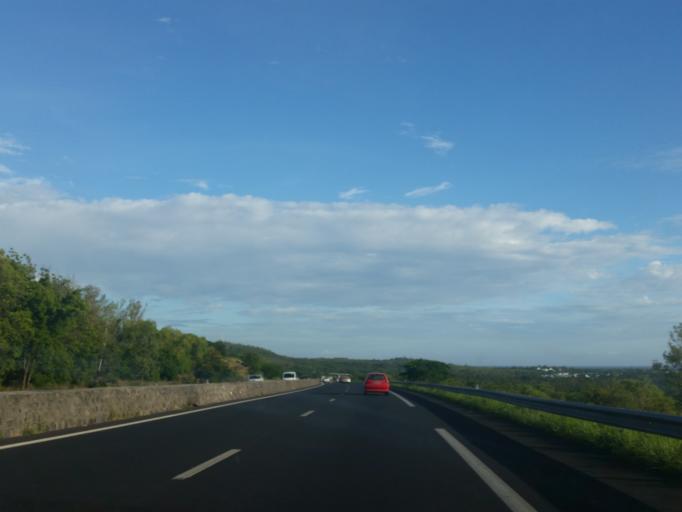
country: RE
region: Reunion
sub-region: Reunion
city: Les Avirons
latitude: -21.2529
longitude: 55.3284
